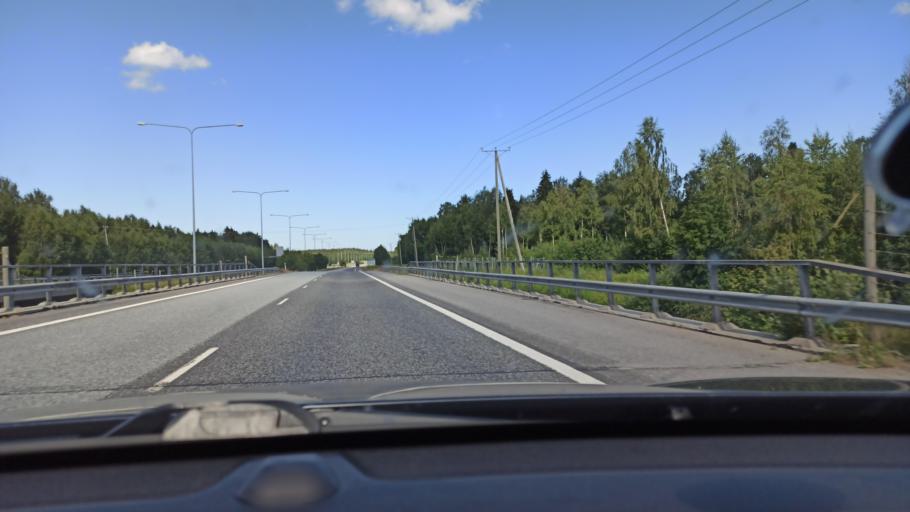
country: FI
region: Ostrobothnia
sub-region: Vaasa
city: Ristinummi
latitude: 63.0401
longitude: 21.7327
